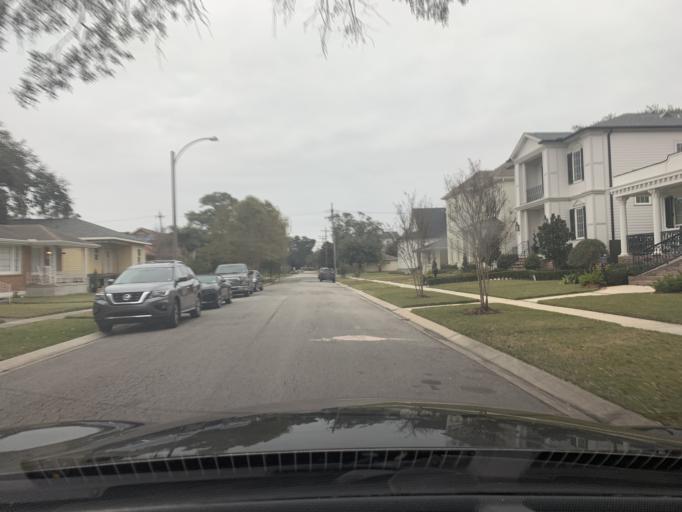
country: US
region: Louisiana
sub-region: Jefferson Parish
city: Metairie
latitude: 30.0166
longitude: -90.1034
